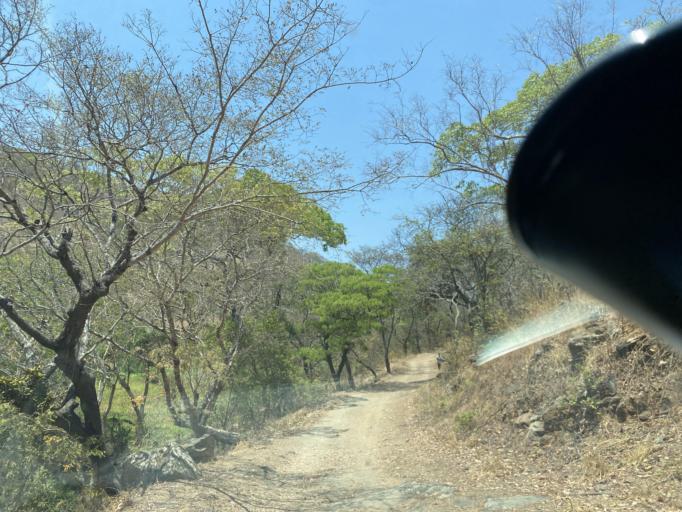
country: ZM
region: Lusaka
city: Kafue
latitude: -15.8044
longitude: 28.4257
